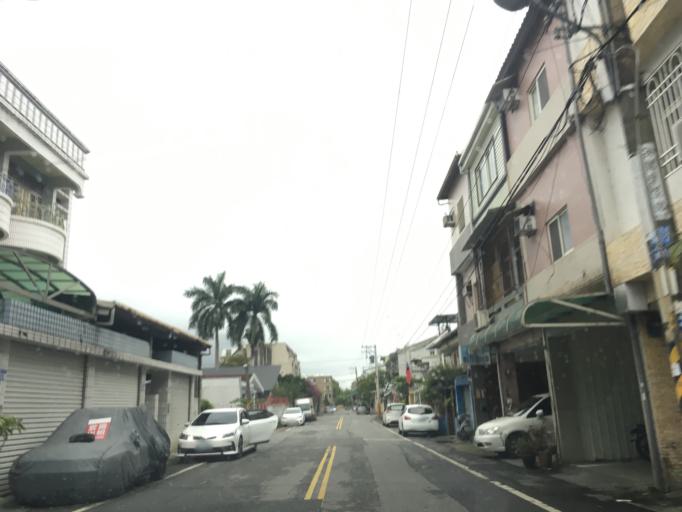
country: TW
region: Taiwan
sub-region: Hualien
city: Hualian
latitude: 23.9942
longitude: 121.5733
